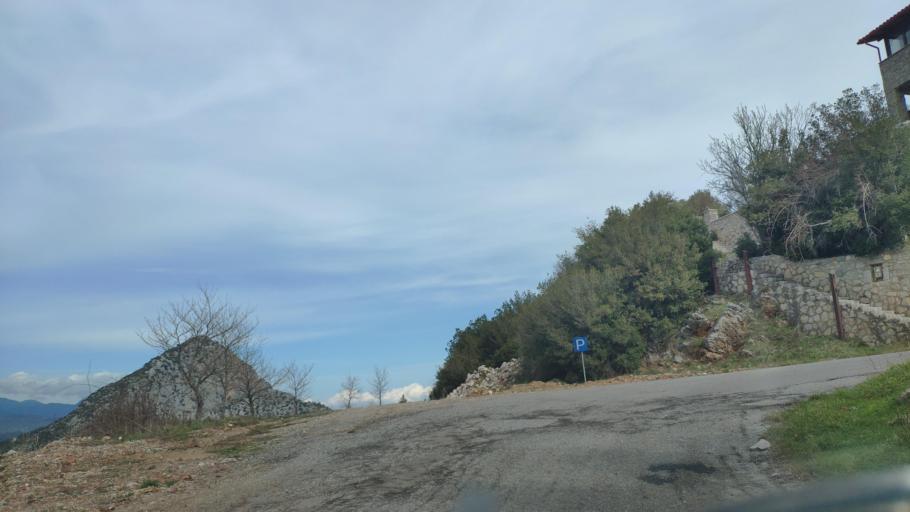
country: GR
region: Central Greece
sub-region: Nomos Fokidos
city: Amfissa
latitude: 38.6430
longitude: 22.4226
